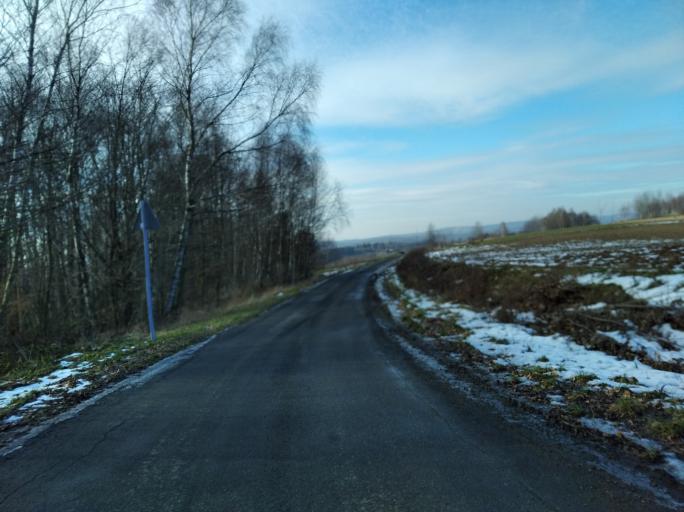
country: PL
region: Subcarpathian Voivodeship
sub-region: Powiat strzyzowski
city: Gwoznica Gorna
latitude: 49.8233
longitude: 21.9857
